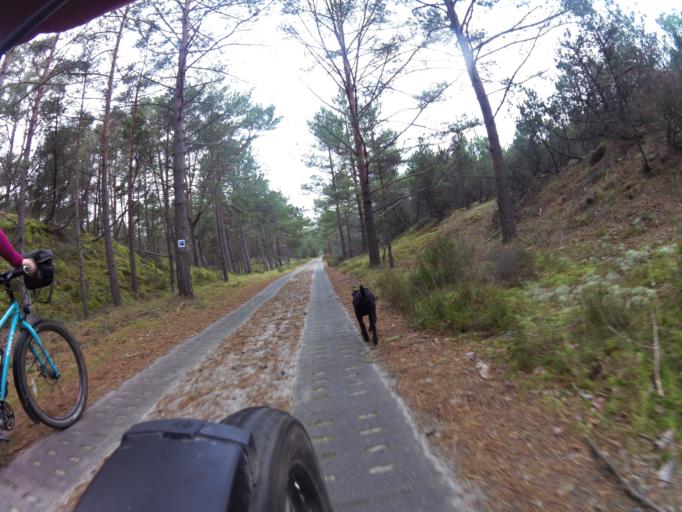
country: PL
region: Pomeranian Voivodeship
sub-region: Powiat pucki
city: Hel
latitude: 54.6250
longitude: 18.8165
